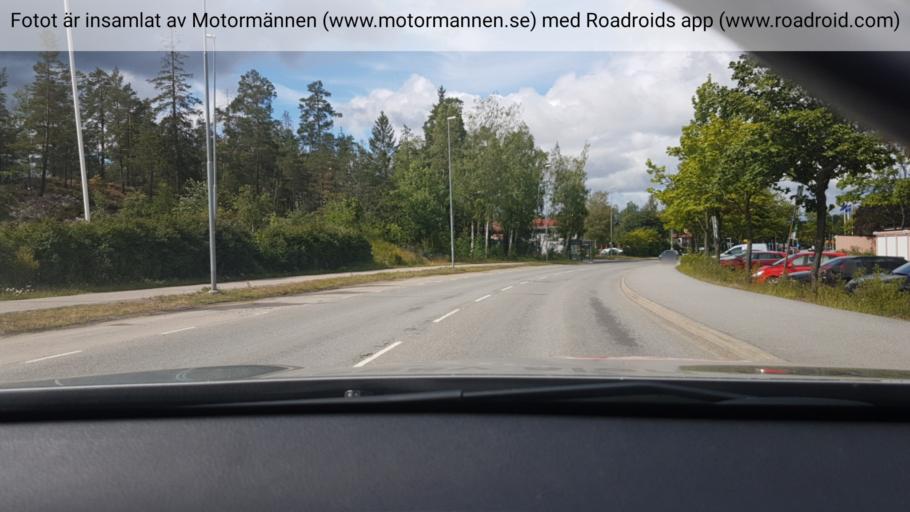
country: SE
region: Stockholm
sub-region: Tyreso Kommun
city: Bollmora
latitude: 59.2413
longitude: 18.2155
